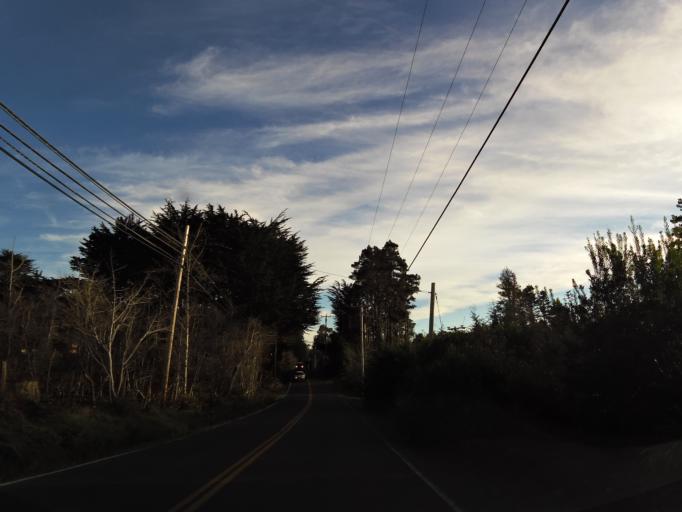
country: US
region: California
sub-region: Mendocino County
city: Fort Bragg
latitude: 39.3392
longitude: -123.8093
